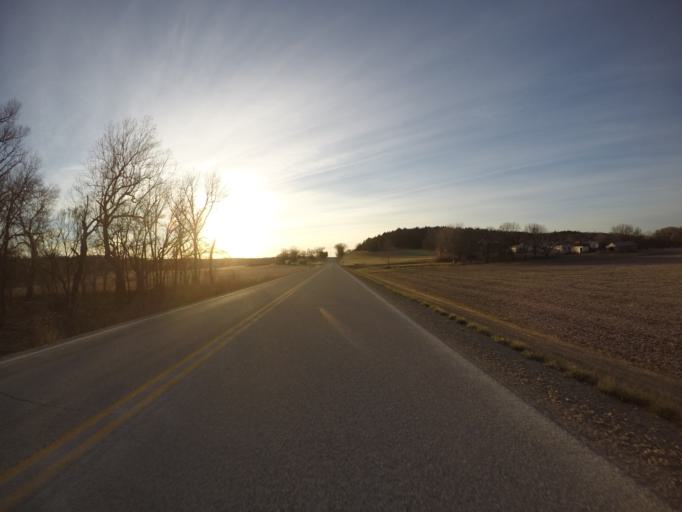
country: US
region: Kansas
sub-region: Riley County
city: Manhattan
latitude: 39.3051
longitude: -96.7210
